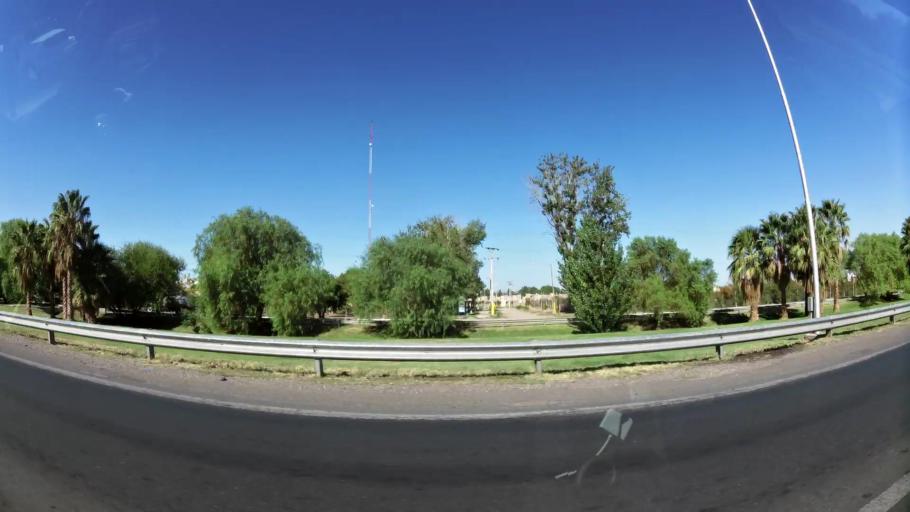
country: AR
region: San Juan
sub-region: Departamento de Santa Lucia
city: Santa Lucia
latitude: -31.5262
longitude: -68.5032
